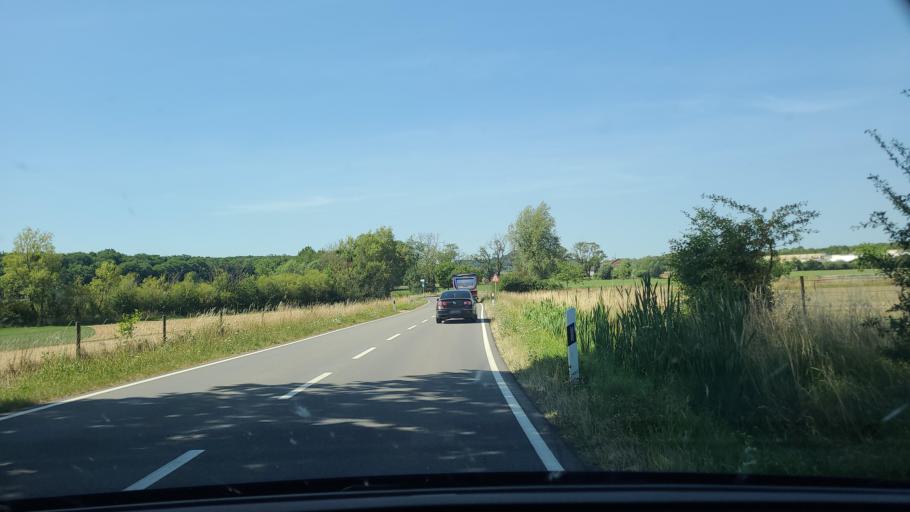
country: LU
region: Luxembourg
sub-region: Canton d'Esch-sur-Alzette
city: Mondercange
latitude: 49.5466
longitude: 5.9621
